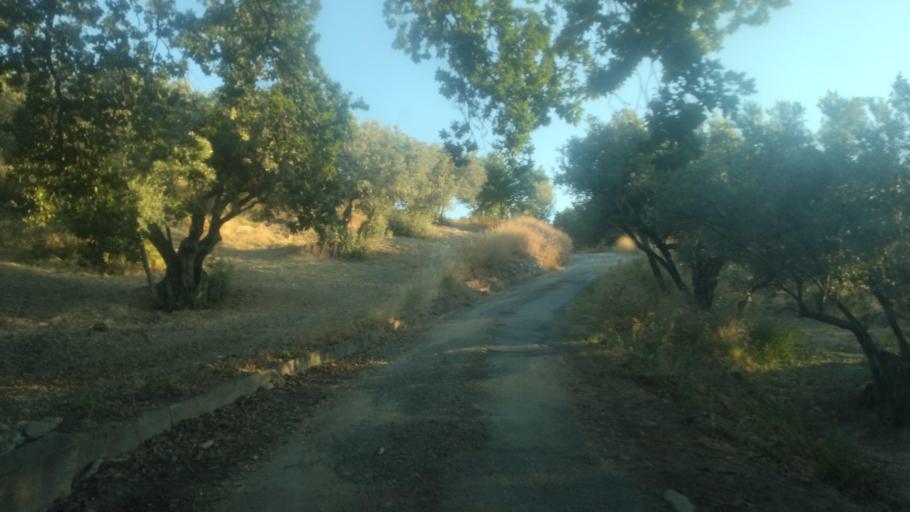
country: IT
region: Calabria
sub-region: Provincia di Catanzaro
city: Staletti
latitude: 38.7740
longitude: 16.5467
